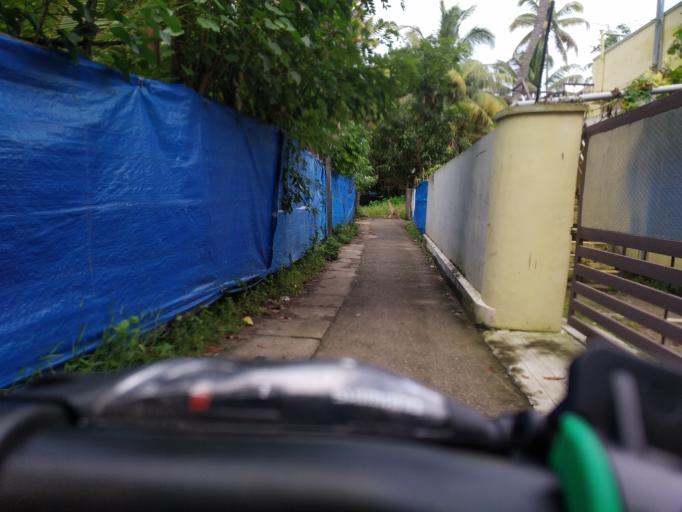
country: IN
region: Kerala
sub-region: Ernakulam
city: Elur
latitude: 10.0764
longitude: 76.2156
